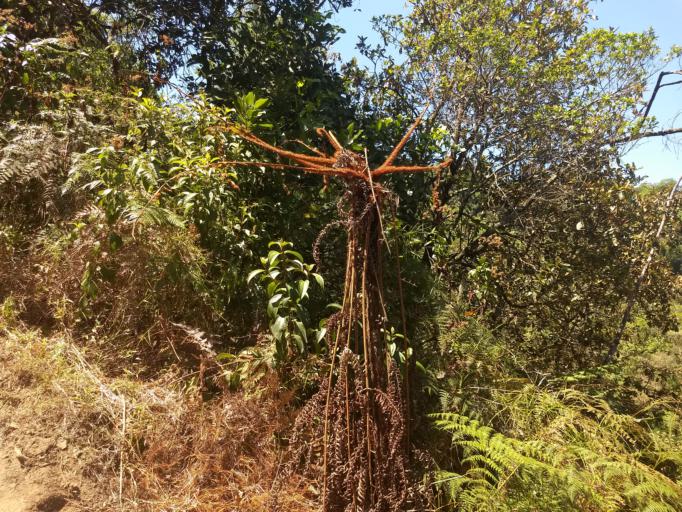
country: MX
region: Puebla
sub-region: Cuetzalan del Progreso
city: Ciudad de Cuetzalan
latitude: 20.0094
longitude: -97.5047
